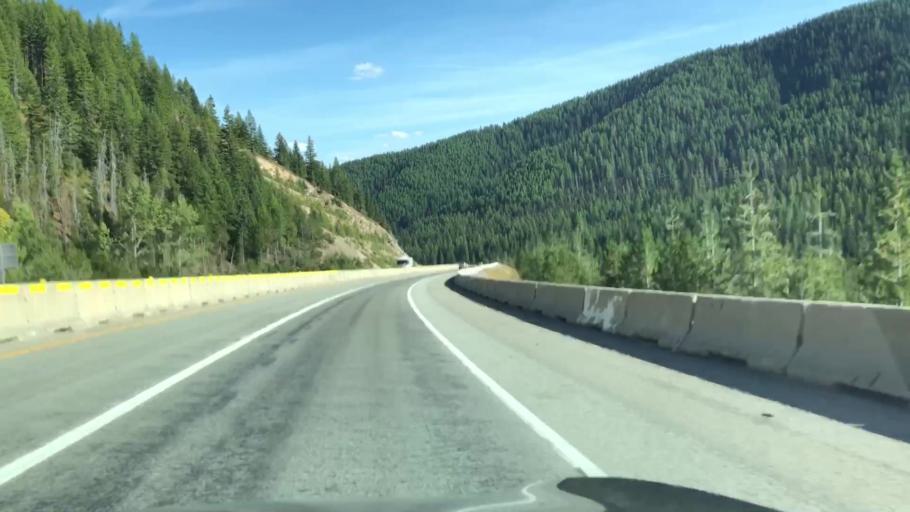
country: US
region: Idaho
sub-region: Shoshone County
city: Wallace
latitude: 47.4403
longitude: -115.6854
